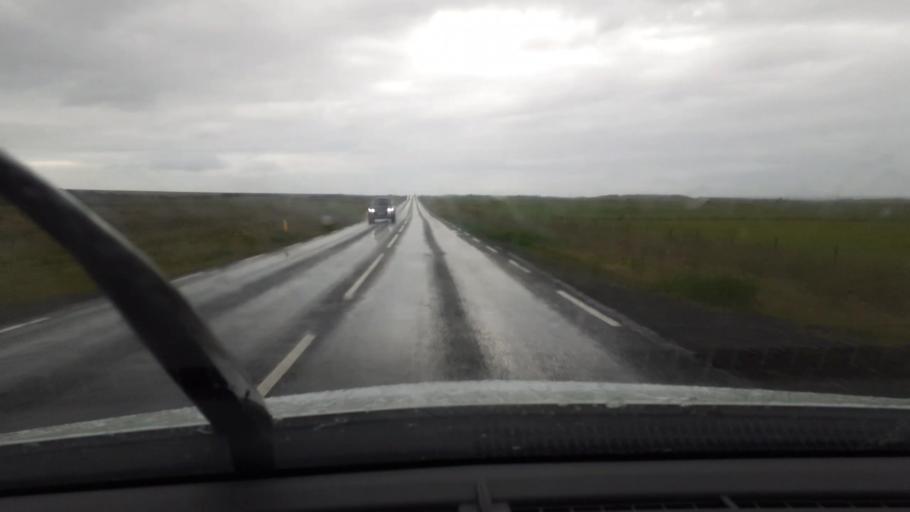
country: IS
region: West
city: Akranes
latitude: 64.3638
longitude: -21.9462
